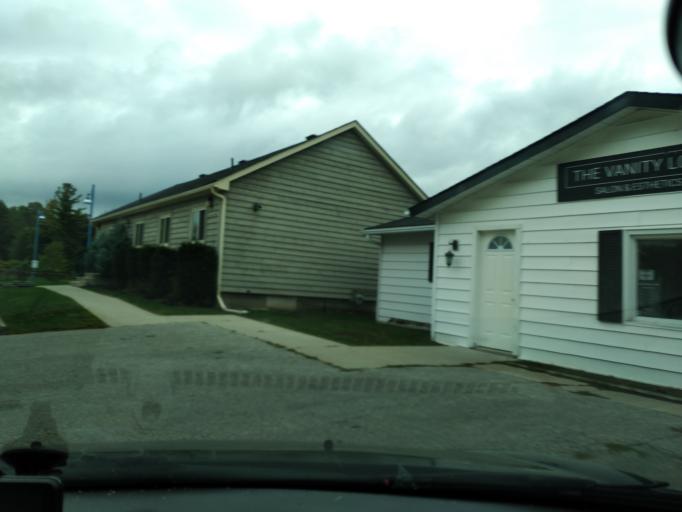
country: CA
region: Ontario
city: Keswick
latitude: 44.3159
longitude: -79.5412
